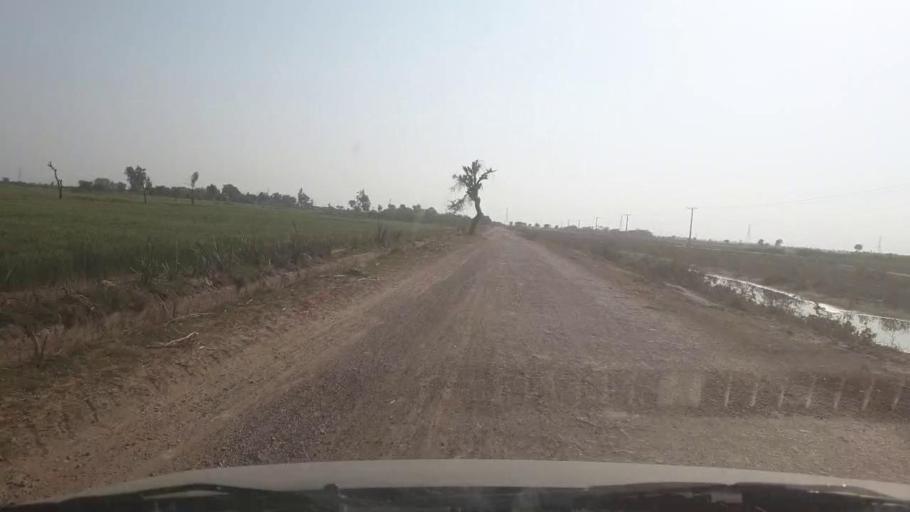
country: PK
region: Sindh
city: Samaro
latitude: 25.1449
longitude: 69.3794
